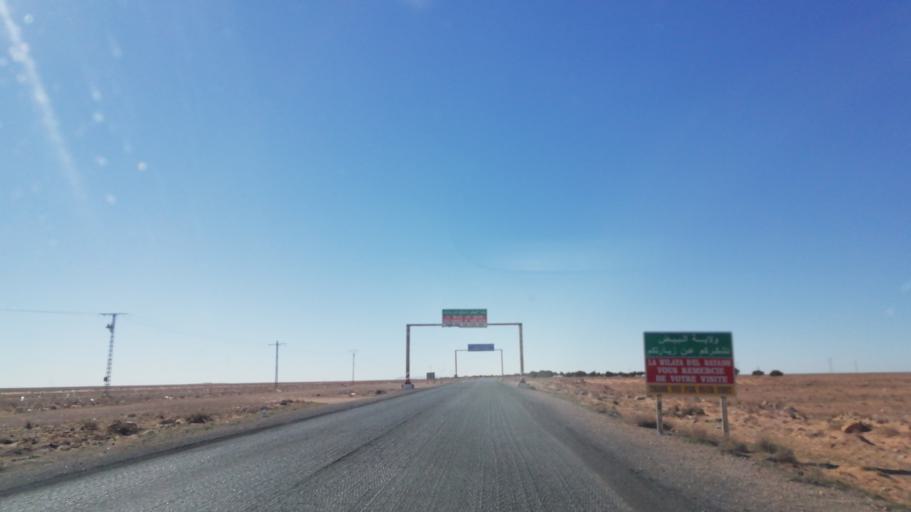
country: DZ
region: Saida
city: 'Ain el Hadjar
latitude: 34.0075
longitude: 0.0501
